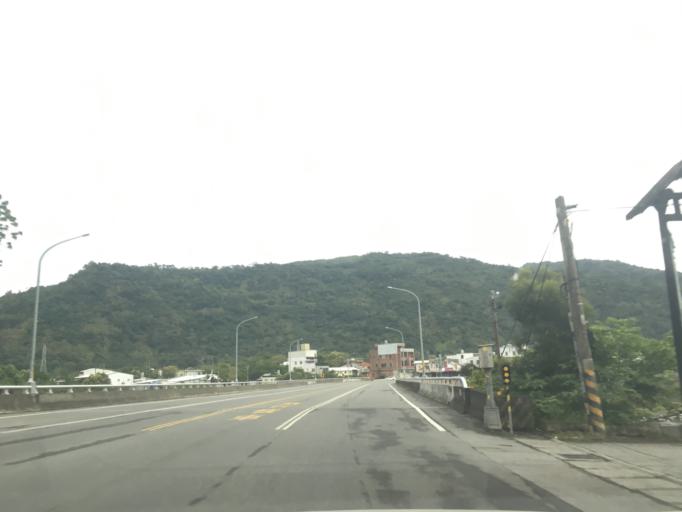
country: TW
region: Taiwan
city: Taitung City
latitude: 22.7601
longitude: 121.0495
